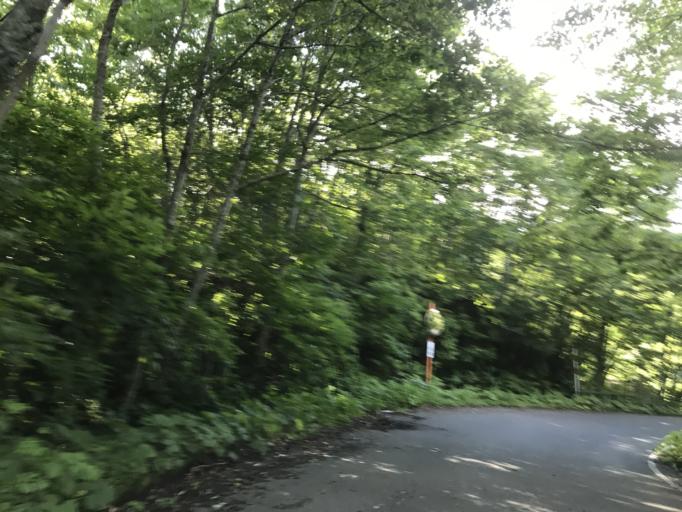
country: JP
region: Iwate
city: Ichinoseki
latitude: 38.9157
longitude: 140.8286
